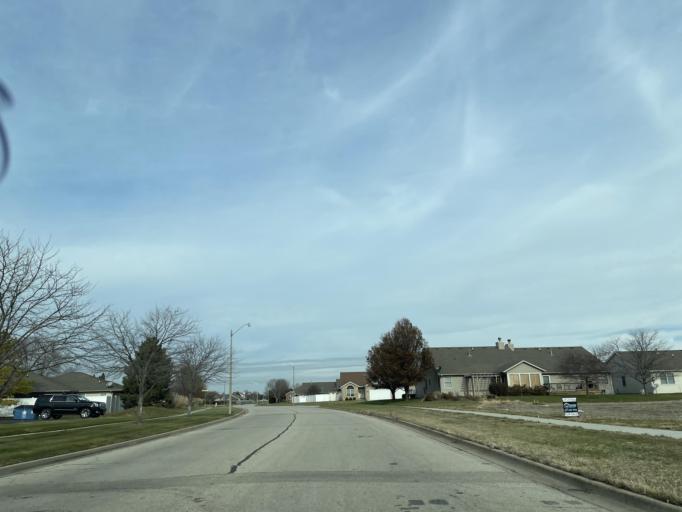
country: US
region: Illinois
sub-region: Sangamon County
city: Jerome
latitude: 39.7596
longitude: -89.7291
